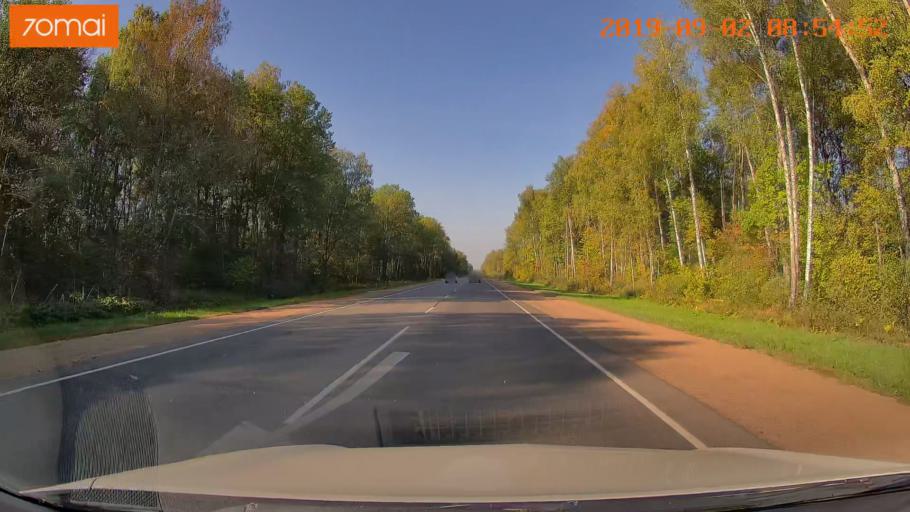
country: RU
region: Kaluga
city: Medyn'
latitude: 54.9583
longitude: 35.8297
